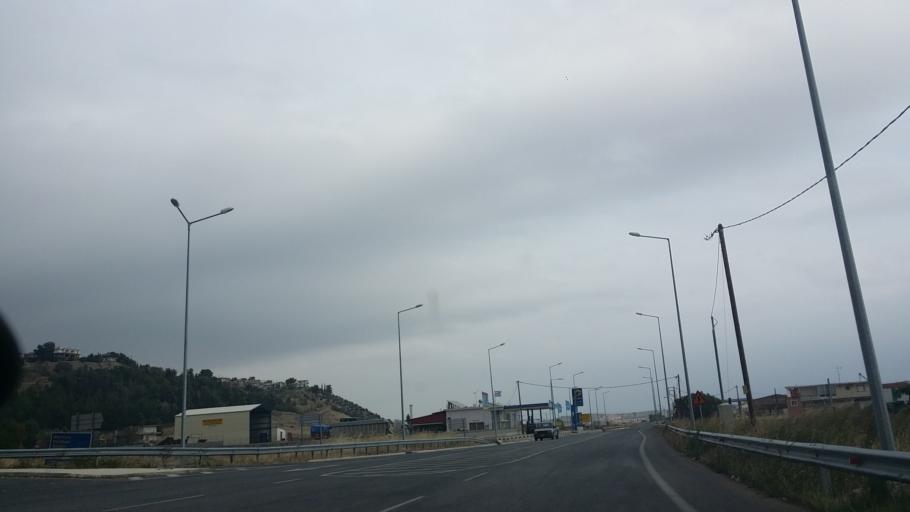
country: GR
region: Central Greece
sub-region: Nomos Voiotias
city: Thespies
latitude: 38.2984
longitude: 23.1416
